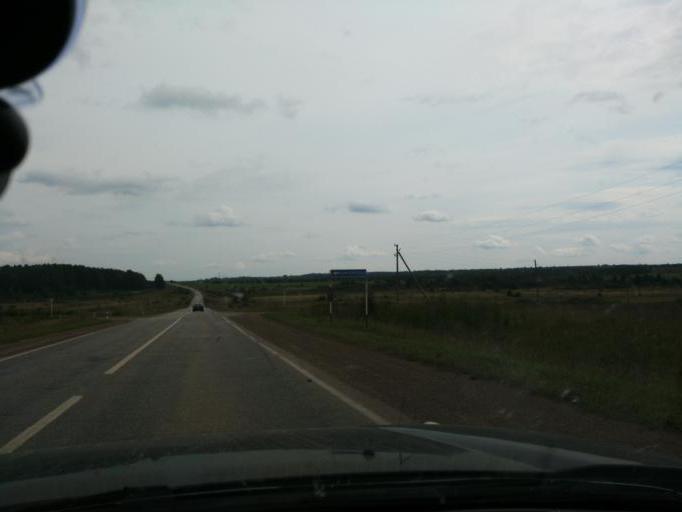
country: RU
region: Perm
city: Kuyeda
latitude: 56.4696
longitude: 55.7148
